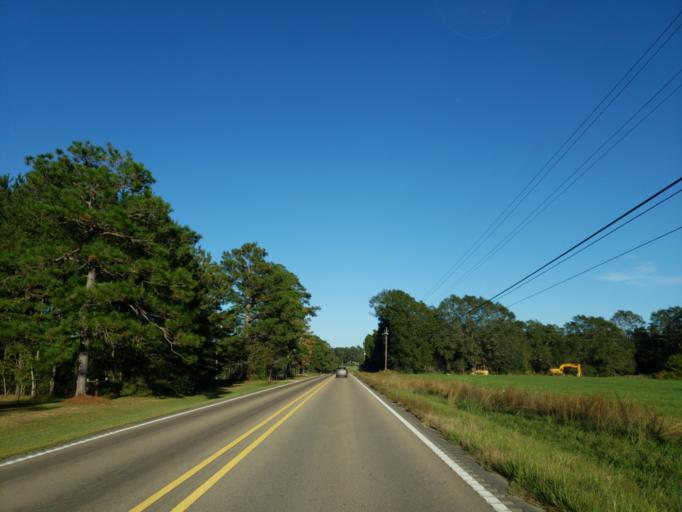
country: US
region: Mississippi
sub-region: Perry County
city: Richton
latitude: 31.3661
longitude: -88.8814
